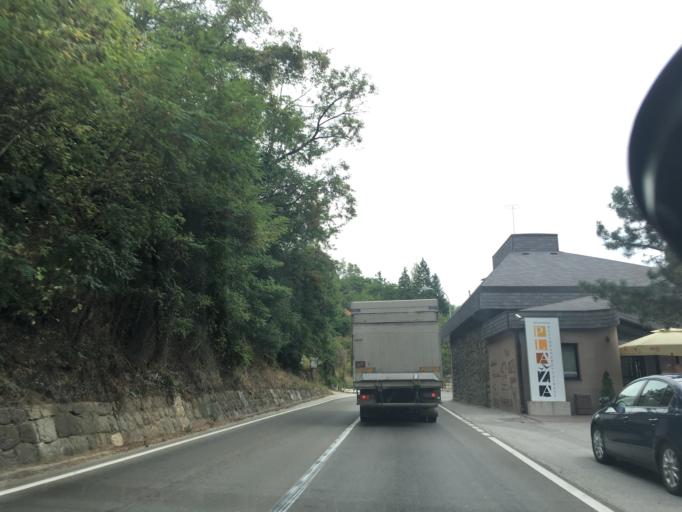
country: RS
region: Central Serbia
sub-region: Moravicki Okrug
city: Lucani
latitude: 43.9104
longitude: 20.2322
